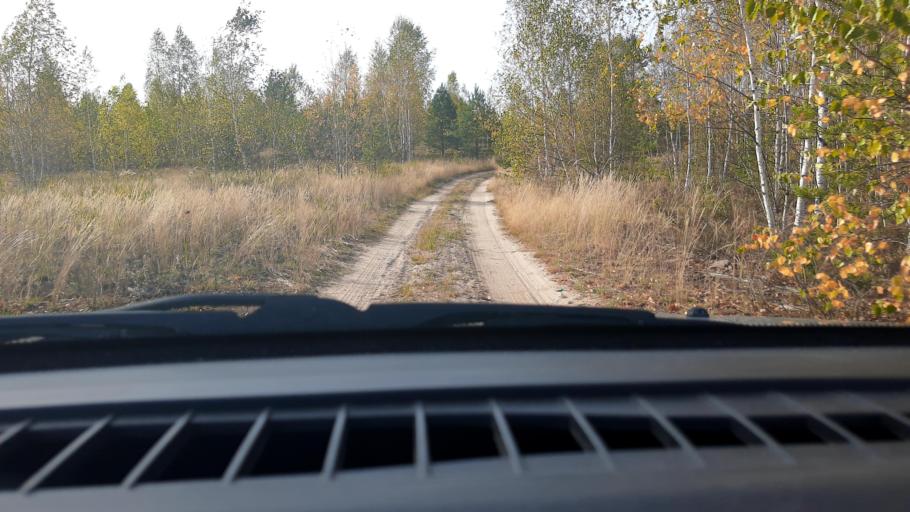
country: RU
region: Nizjnij Novgorod
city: Lukino
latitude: 56.3915
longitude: 43.6008
